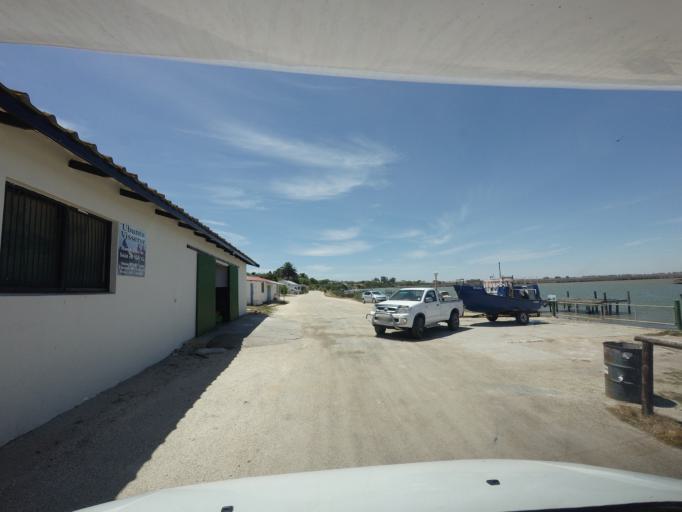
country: ZA
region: Western Cape
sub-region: West Coast District Municipality
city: Vredenburg
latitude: -32.7875
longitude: 18.1874
